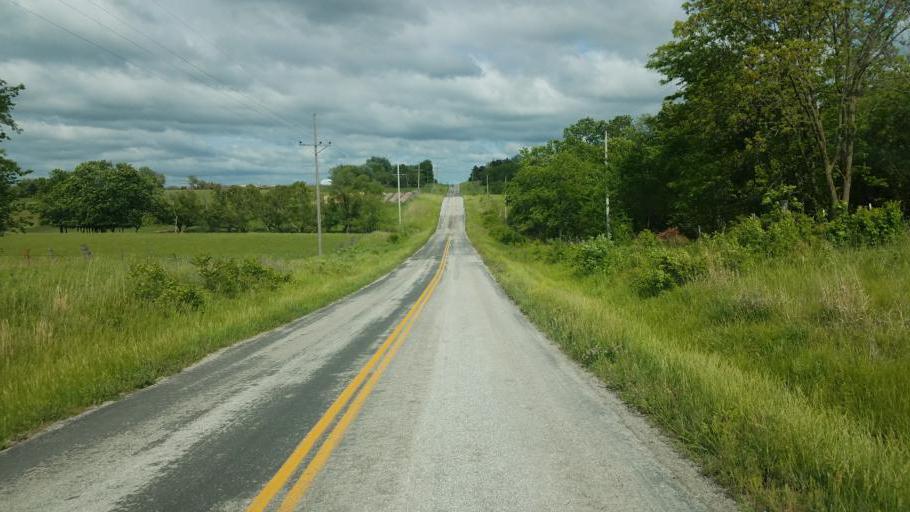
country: US
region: Missouri
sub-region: Mercer County
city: Princeton
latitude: 40.3000
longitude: -93.7423
